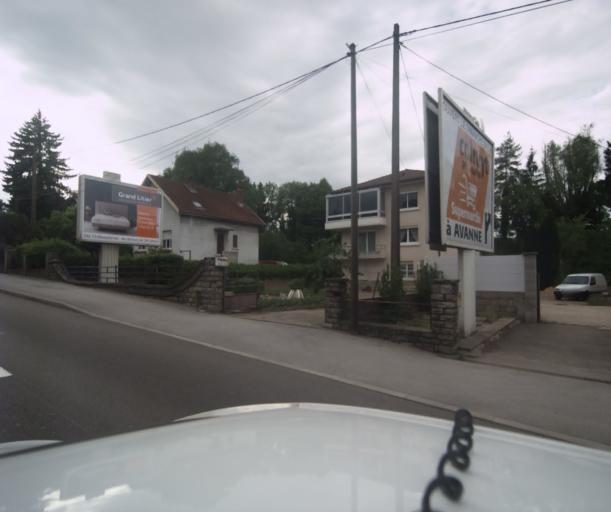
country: FR
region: Franche-Comte
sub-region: Departement du Doubs
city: Avanne-Aveney
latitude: 47.2261
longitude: 5.9767
